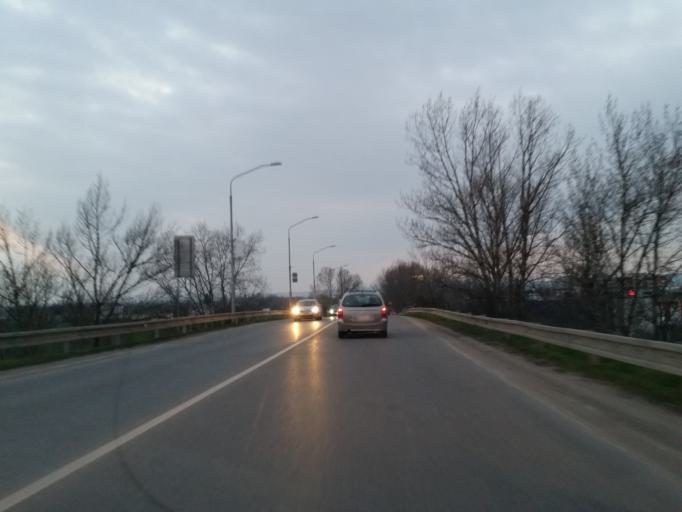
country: SK
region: Trnavsky
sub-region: Okres Trnava
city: Piestany
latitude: 48.5890
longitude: 17.8094
